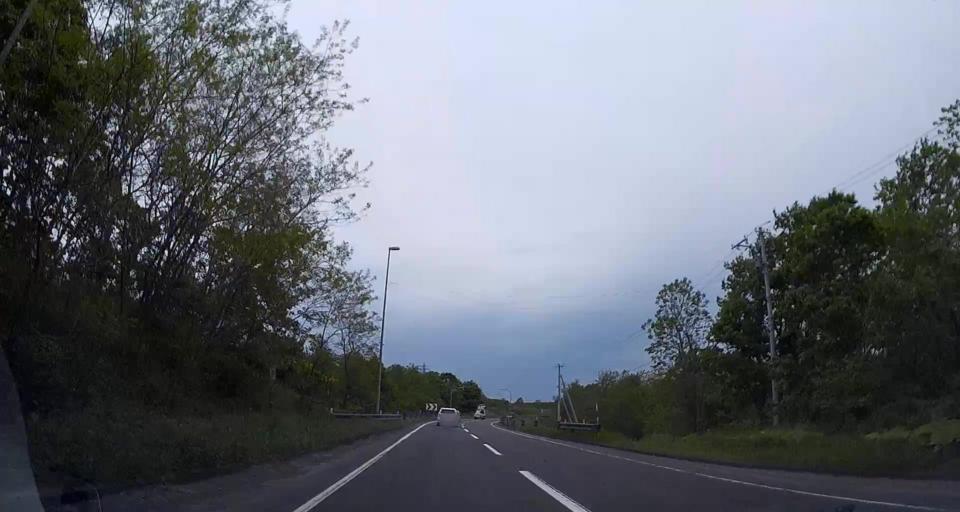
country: JP
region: Hokkaido
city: Chitose
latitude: 42.7003
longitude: 141.7419
